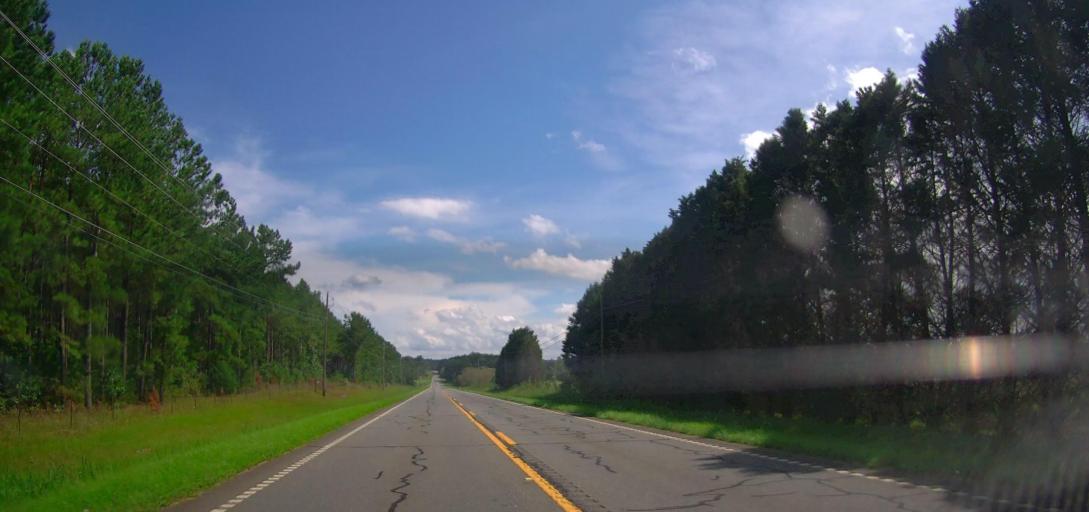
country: US
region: Georgia
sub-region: Meriwether County
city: Manchester
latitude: 32.8359
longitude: -84.6210
